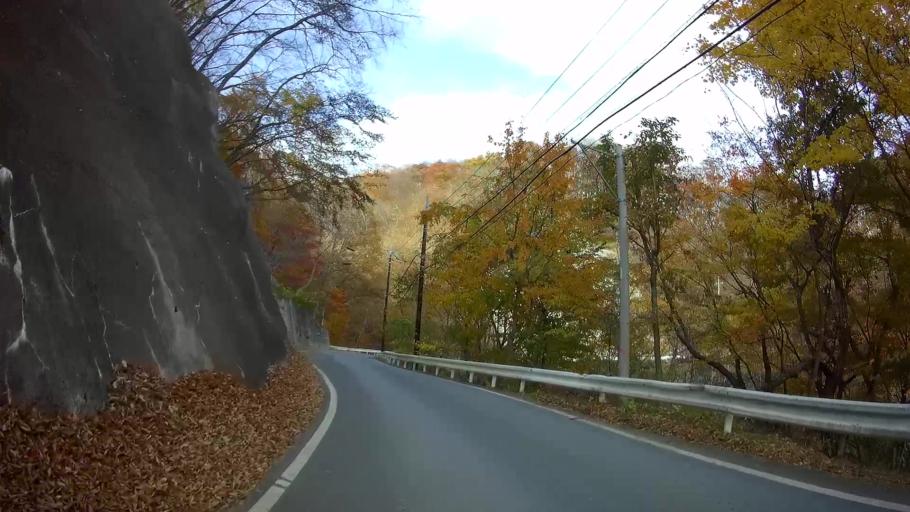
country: JP
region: Gunma
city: Nakanojomachi
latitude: 36.6640
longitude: 138.6679
